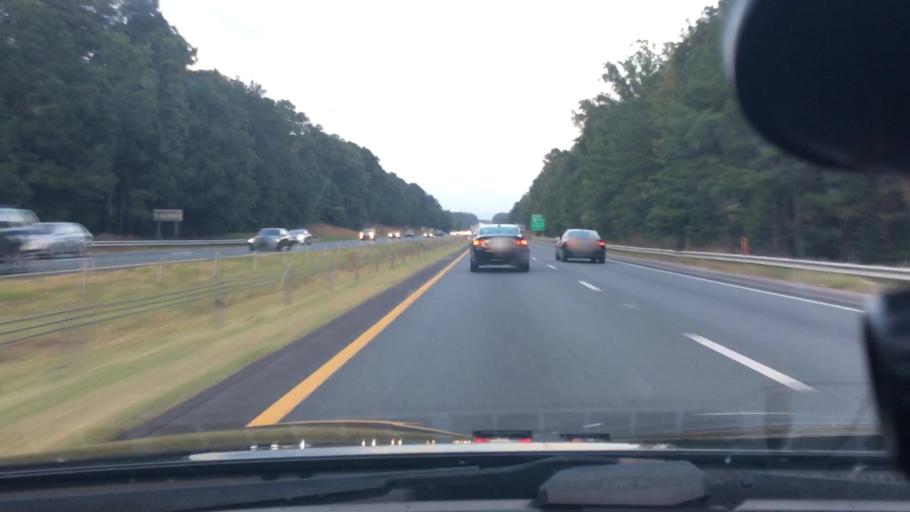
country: US
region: North Carolina
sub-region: Wake County
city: Apex
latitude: 35.7293
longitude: -78.8076
